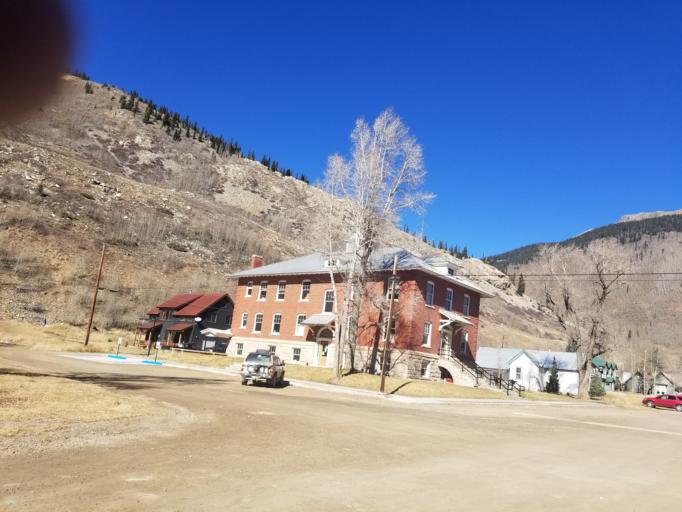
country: US
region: Colorado
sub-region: San Juan County
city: Silverton
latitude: 37.8134
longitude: -107.6654
